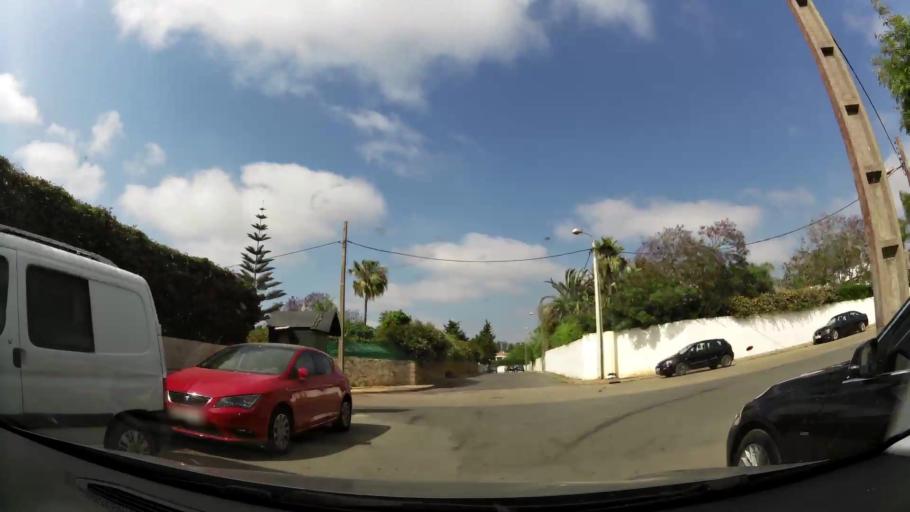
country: MA
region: Rabat-Sale-Zemmour-Zaer
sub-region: Rabat
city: Rabat
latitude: 33.9758
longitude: -6.8436
